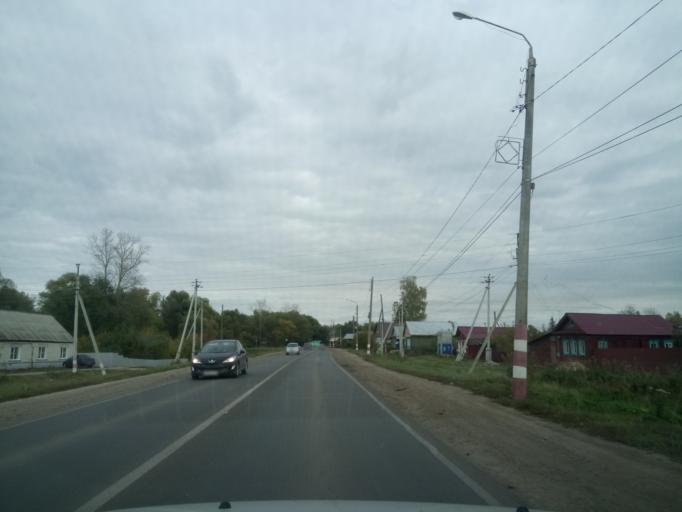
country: RU
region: Nizjnij Novgorod
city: Lukoyanov
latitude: 55.0308
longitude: 44.4787
